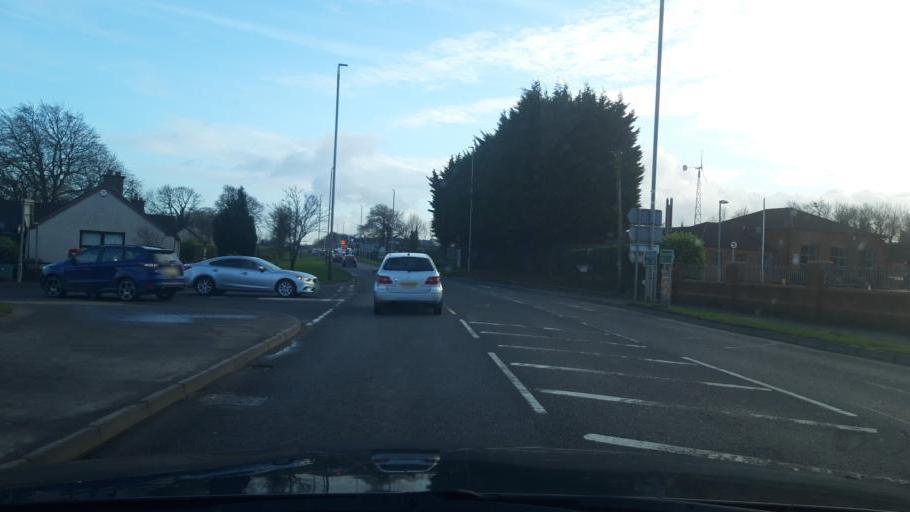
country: GB
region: Northern Ireland
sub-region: Dungannon District
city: Dungannon
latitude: 54.4886
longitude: -6.7471
